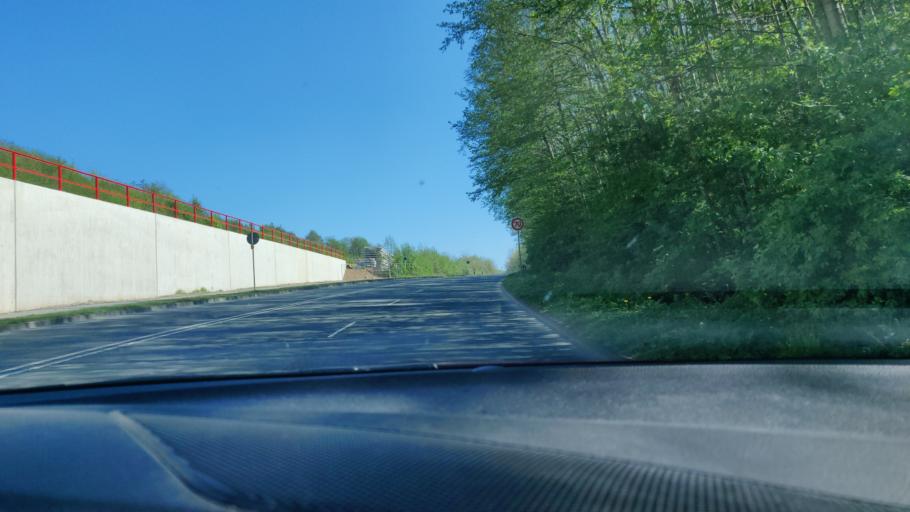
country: DE
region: North Rhine-Westphalia
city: Wulfrath
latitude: 51.2518
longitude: 7.0501
